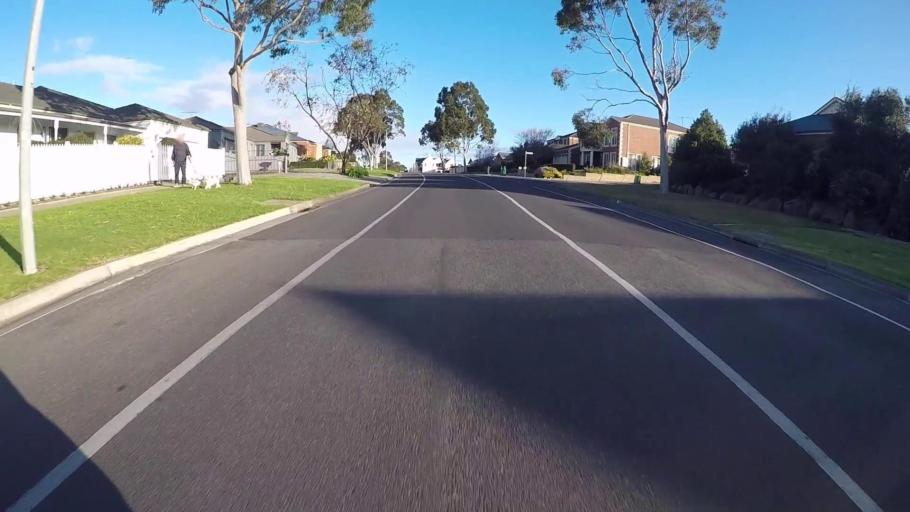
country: AU
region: Victoria
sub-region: Greater Geelong
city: Wandana Heights
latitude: -38.1645
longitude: 144.3016
